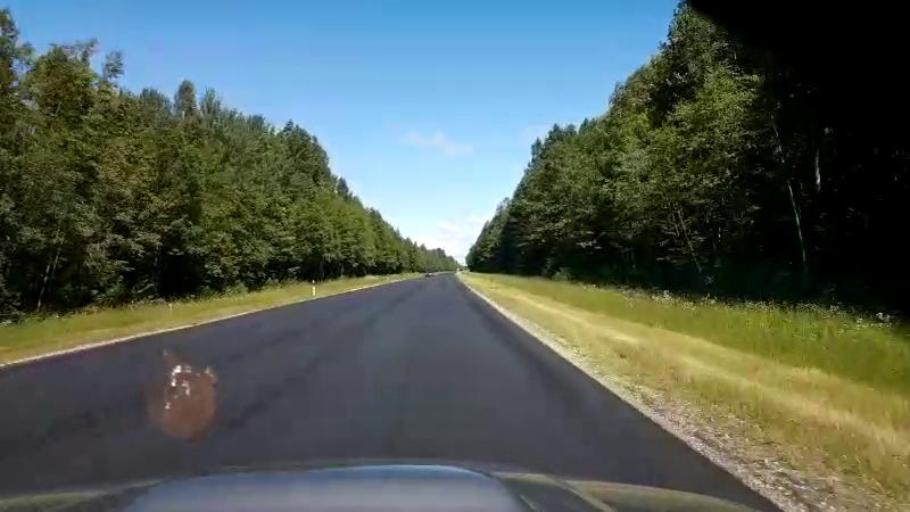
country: LV
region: Salacgrivas
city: Ainazi
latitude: 57.9459
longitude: 24.4342
